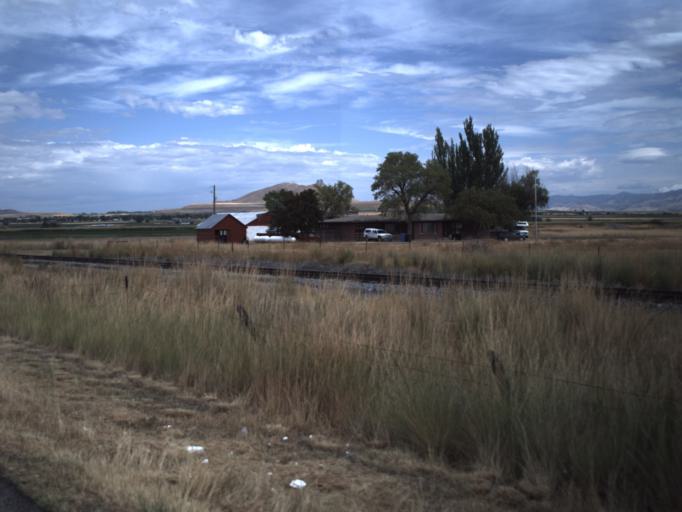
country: US
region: Utah
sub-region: Cache County
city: Benson
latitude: 41.8225
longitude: -111.9989
